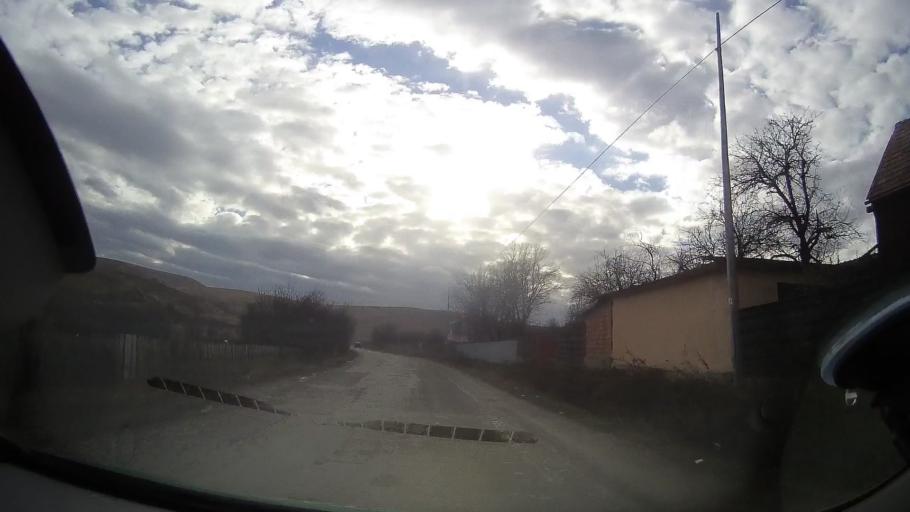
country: RO
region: Cluj
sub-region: Comuna Baisoara
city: Baisoara
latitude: 46.6008
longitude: 23.4622
